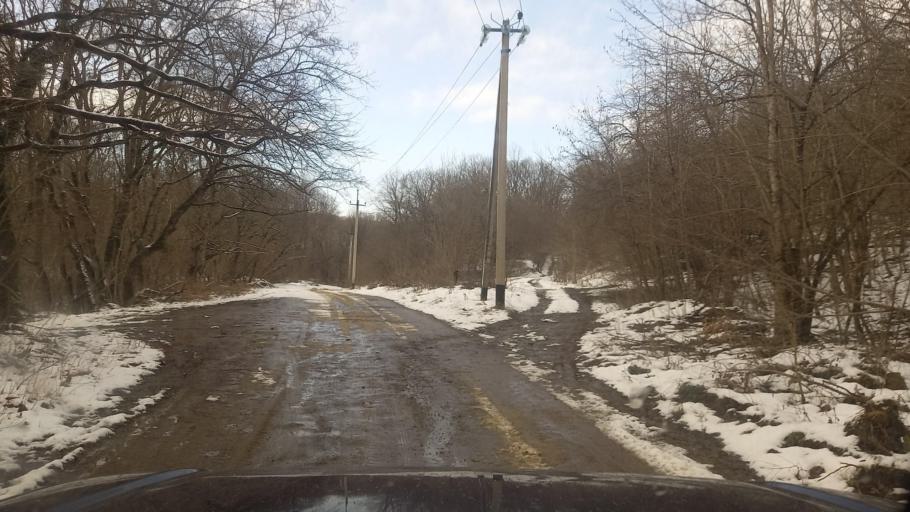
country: RU
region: Krasnodarskiy
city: Smolenskaya
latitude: 44.6978
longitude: 38.8300
